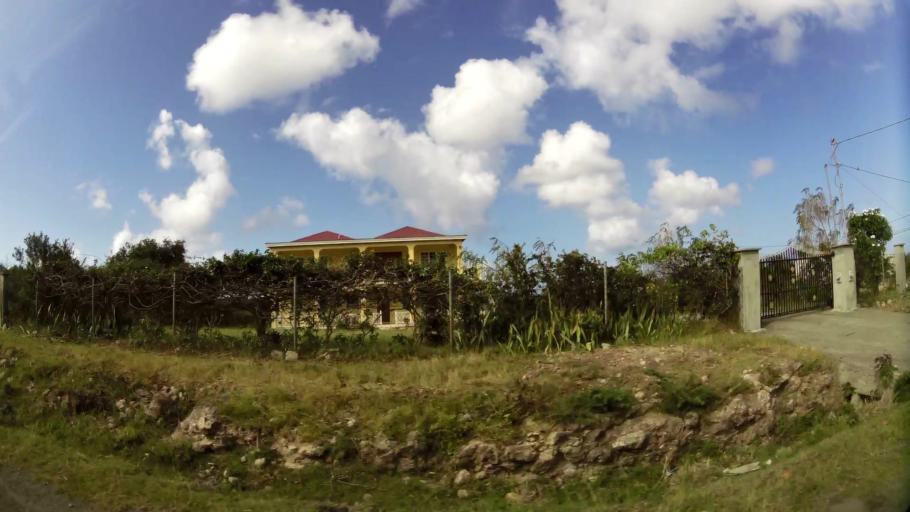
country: KN
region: Saint Paul Charlestown
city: Charlestown
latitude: 17.1248
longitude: -62.6187
